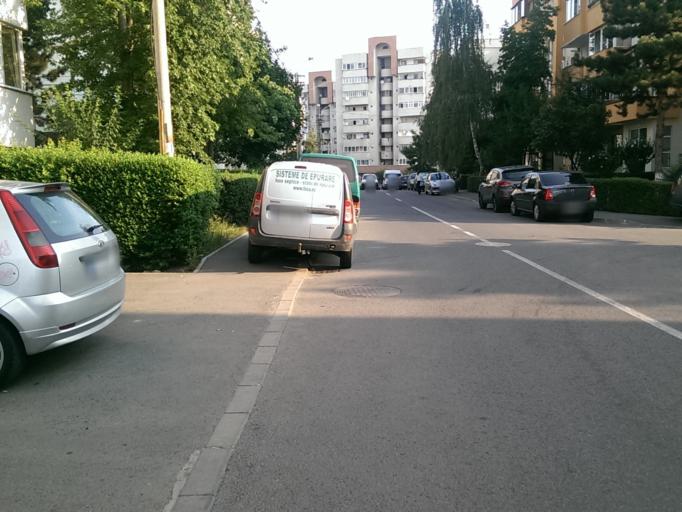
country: RO
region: Cluj
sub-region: Municipiul Cluj-Napoca
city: Cluj-Napoca
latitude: 46.7671
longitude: 23.6177
